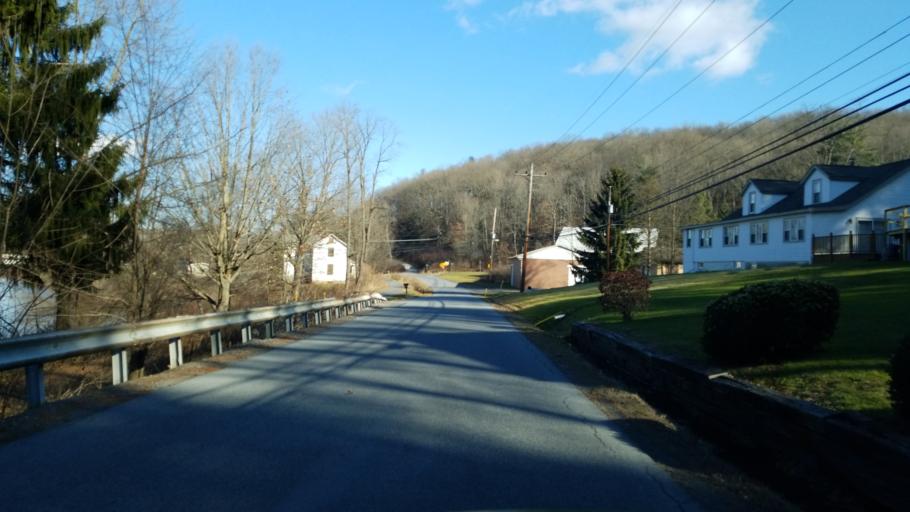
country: US
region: Pennsylvania
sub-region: Clearfield County
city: Hyde
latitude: 40.9925
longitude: -78.4642
